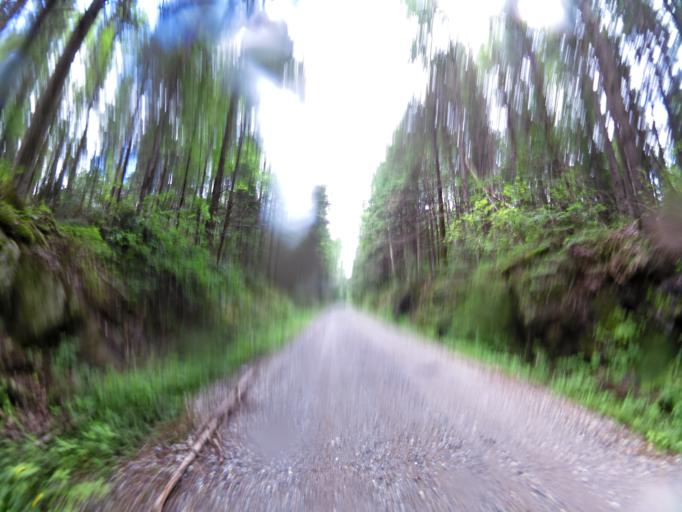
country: CA
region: Ontario
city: Renfrew
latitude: 45.0883
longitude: -76.7206
